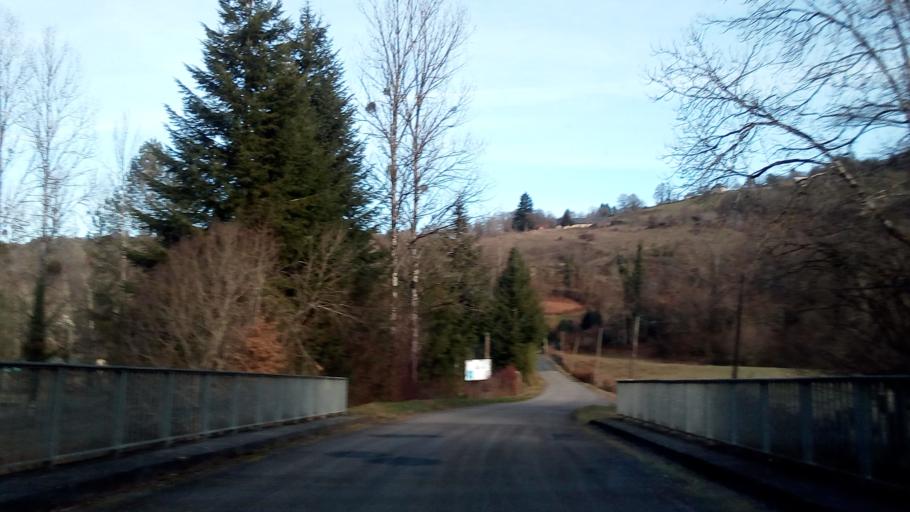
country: FR
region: Limousin
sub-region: Departement de la Correze
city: Naves
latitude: 45.3017
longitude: 1.7972
